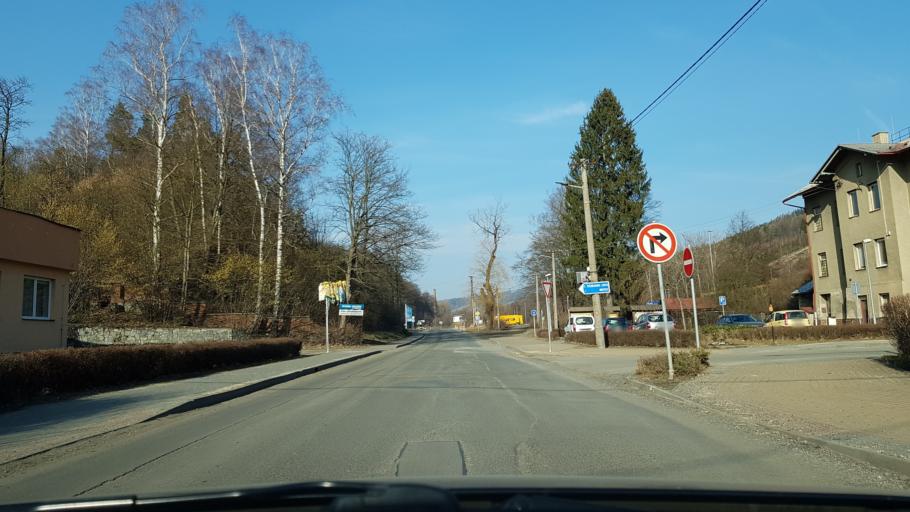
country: CZ
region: Olomoucky
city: Ruda nad Moravou
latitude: 49.9835
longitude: 16.8878
